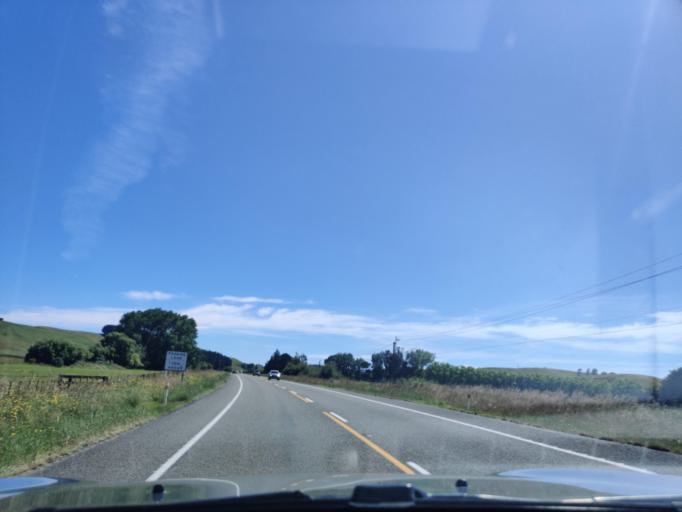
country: NZ
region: Manawatu-Wanganui
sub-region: Rangitikei District
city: Bulls
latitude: -39.9945
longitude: 175.5150
